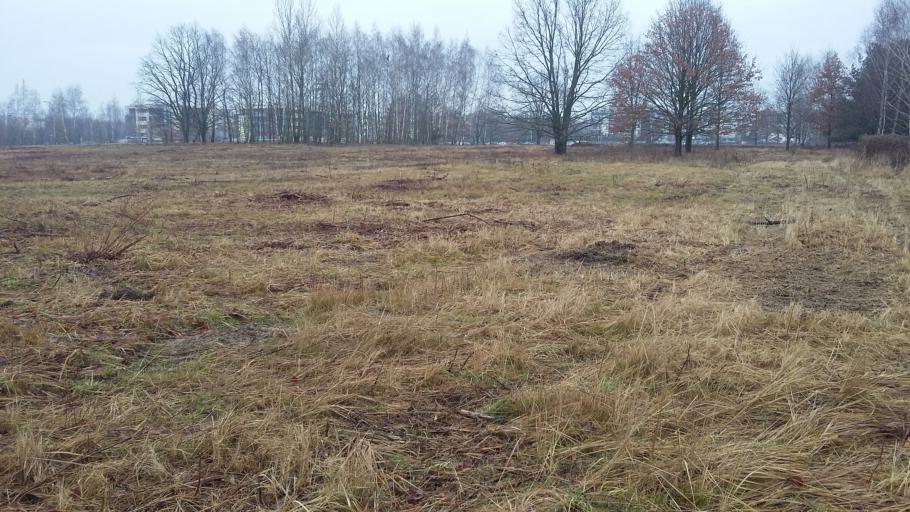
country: PL
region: Lodz Voivodeship
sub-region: Powiat pabianicki
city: Ksawerow
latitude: 51.7322
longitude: 19.4072
